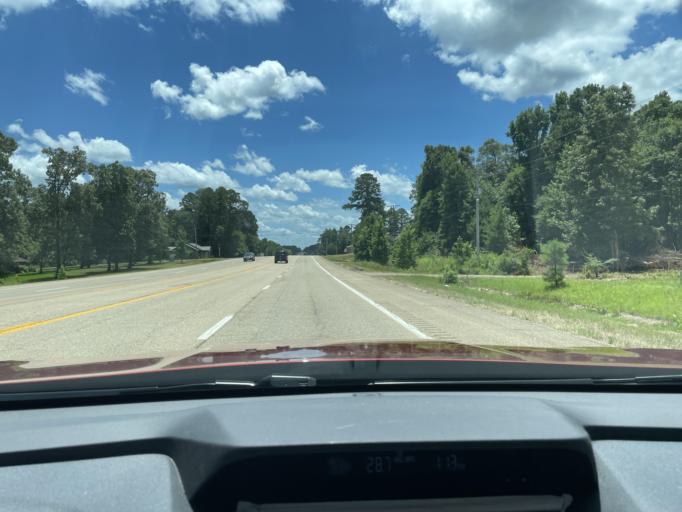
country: US
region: Arkansas
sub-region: Drew County
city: Monticello
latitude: 33.6790
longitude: -91.8051
